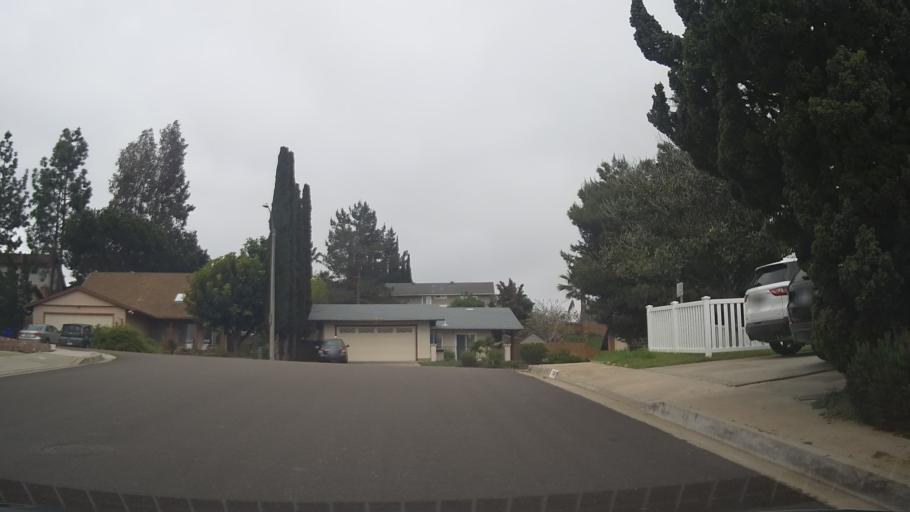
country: US
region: California
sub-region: San Diego County
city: Poway
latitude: 32.9942
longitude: -117.0867
